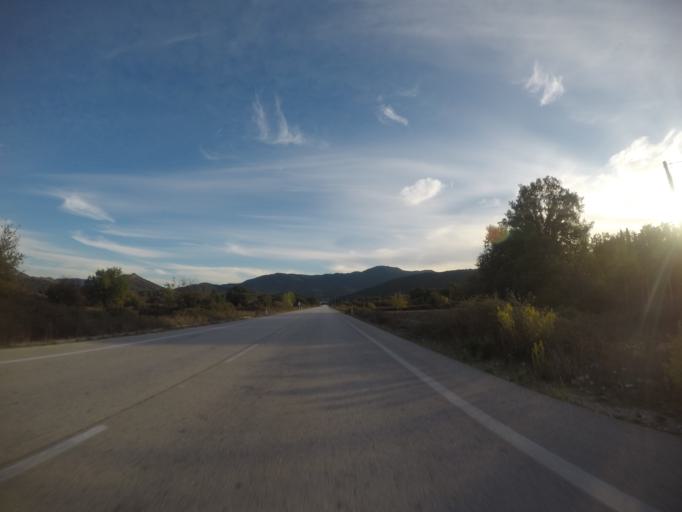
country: GR
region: Epirus
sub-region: Nomos Thesprotias
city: Perdika
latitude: 39.4082
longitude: 20.3805
